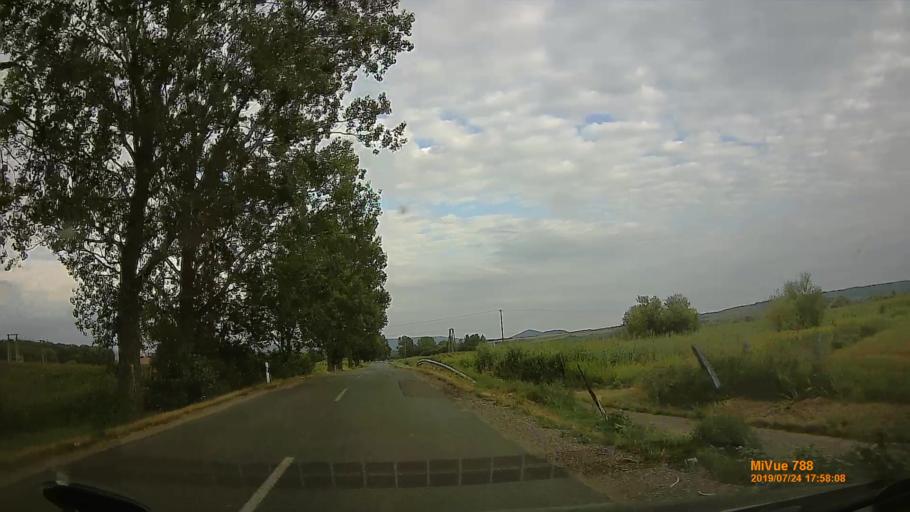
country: HU
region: Borsod-Abauj-Zemplen
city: Encs
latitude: 48.3272
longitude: 21.1437
